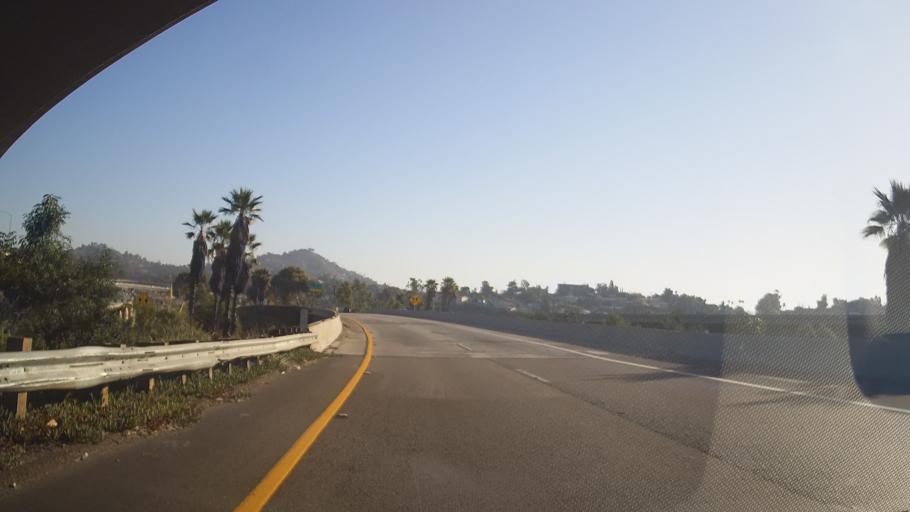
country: US
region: California
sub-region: San Diego County
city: Lemon Grove
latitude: 32.7473
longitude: -117.0185
